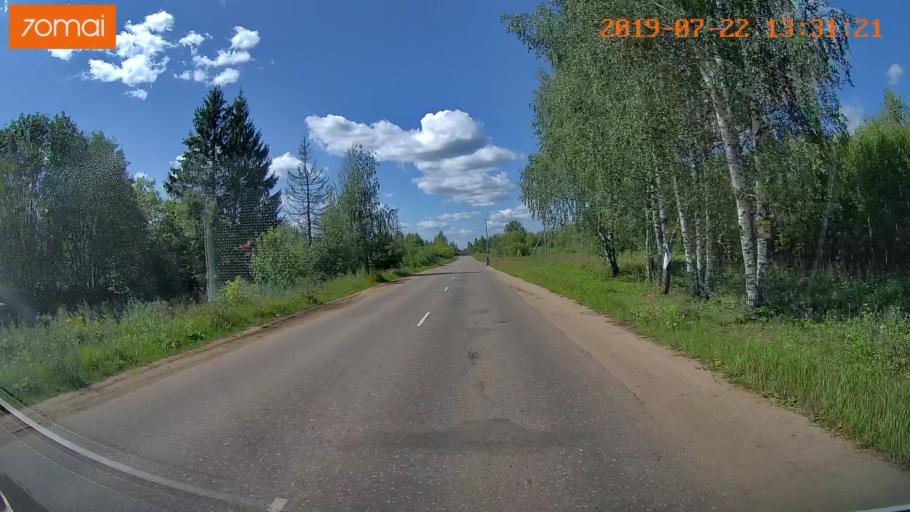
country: RU
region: Ivanovo
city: Novo-Talitsy
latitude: 57.0576
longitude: 40.9170
